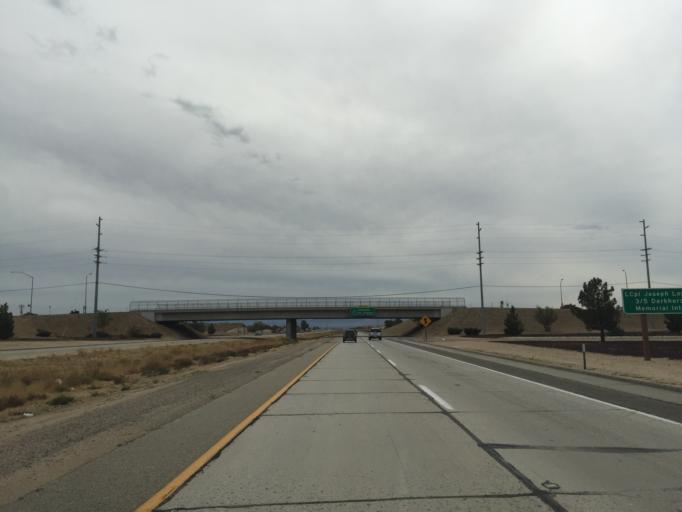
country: US
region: California
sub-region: Kern County
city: Rosamond
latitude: 34.8659
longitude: -118.1718
